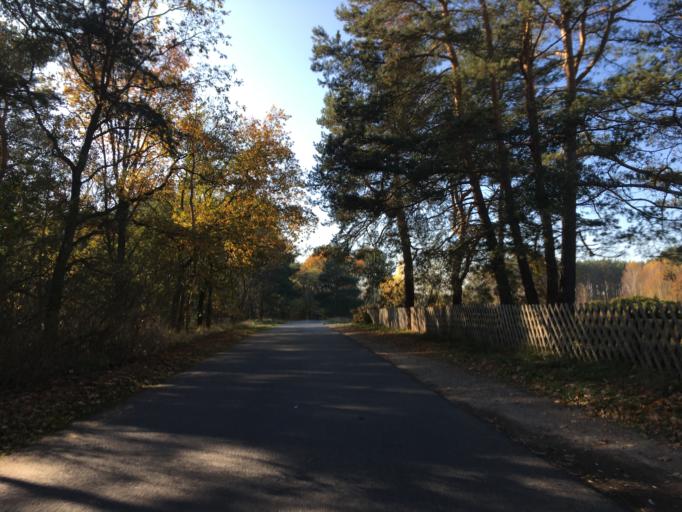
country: DE
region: Brandenburg
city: Spreenhagen
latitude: 52.3397
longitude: 13.9412
